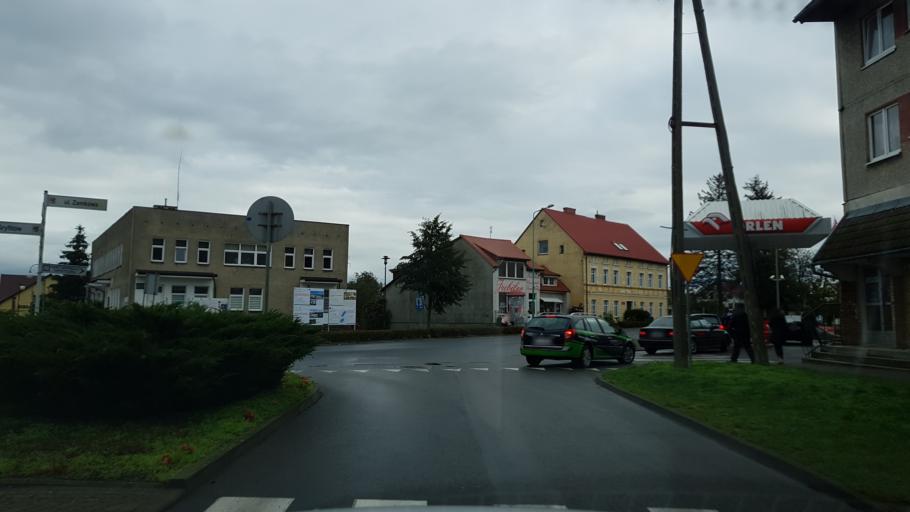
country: PL
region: West Pomeranian Voivodeship
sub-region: Powiat kamienski
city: Wolin
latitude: 53.8452
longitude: 14.6130
